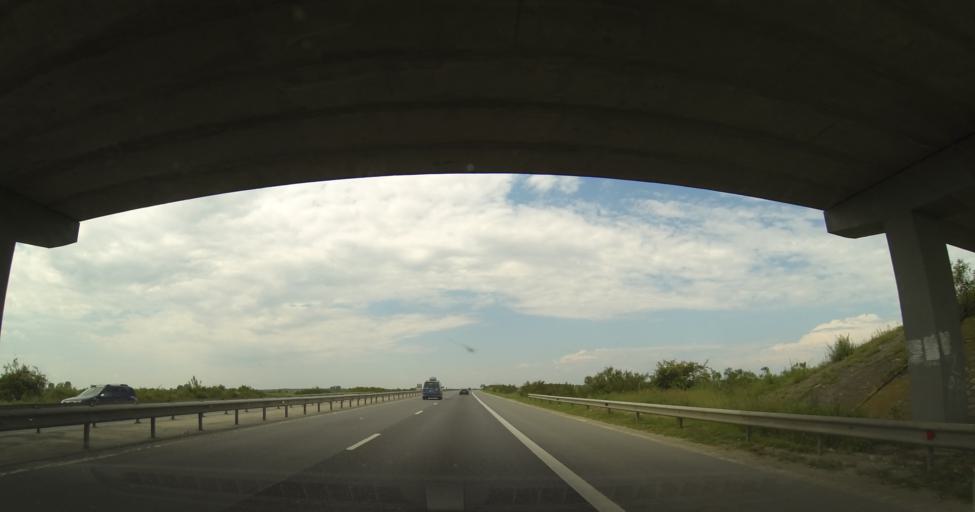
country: RO
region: Dambovita
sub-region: Comuna Mogosani
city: Zavoiu
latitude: 44.6312
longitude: 25.4146
